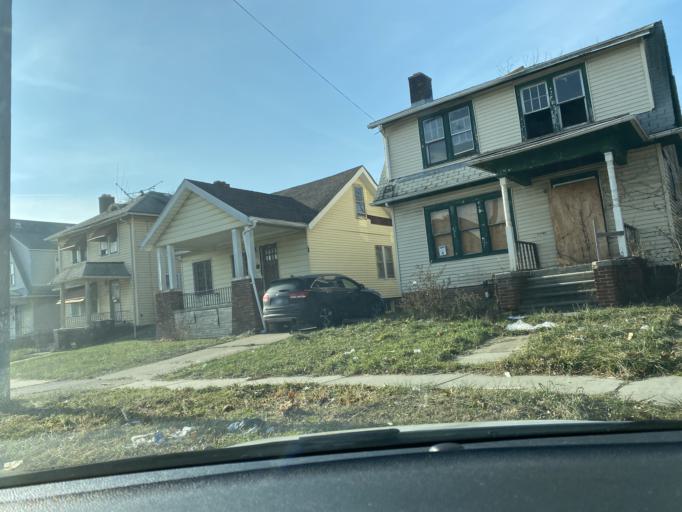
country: US
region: Michigan
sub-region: Wayne County
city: Highland Park
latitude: 42.3852
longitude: -83.1416
